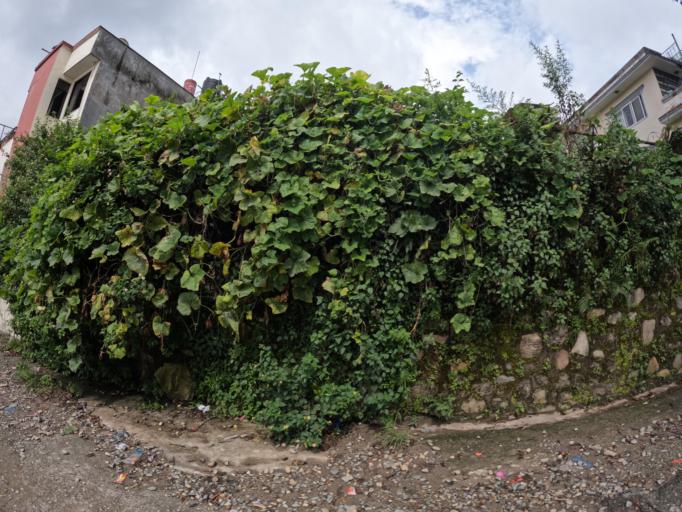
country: NP
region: Central Region
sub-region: Bagmati Zone
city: Kathmandu
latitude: 27.7497
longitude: 85.3197
